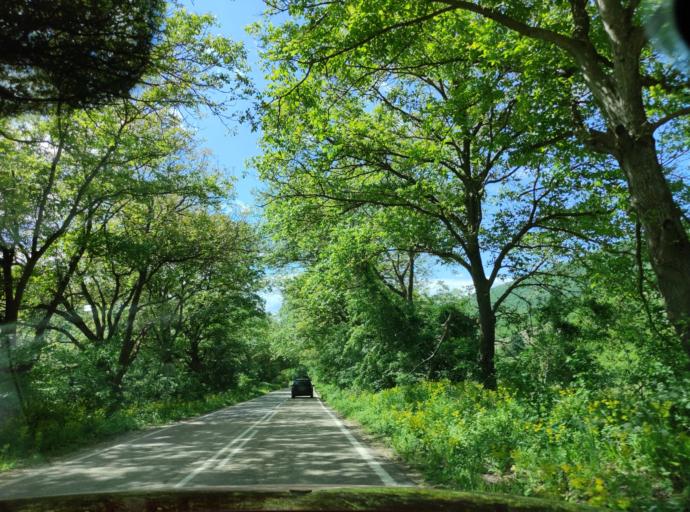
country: BG
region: Montana
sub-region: Obshtina Chiprovtsi
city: Chiprovtsi
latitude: 43.4878
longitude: 22.8141
